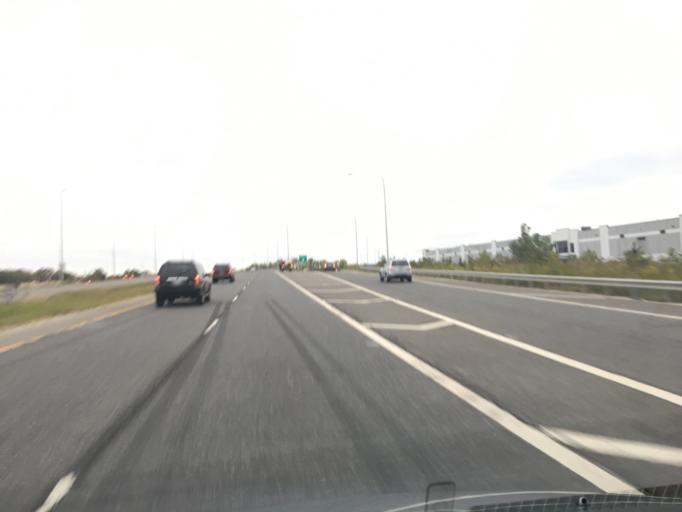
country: US
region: Illinois
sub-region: Cook County
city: Lyons
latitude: 41.8024
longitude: -87.8332
